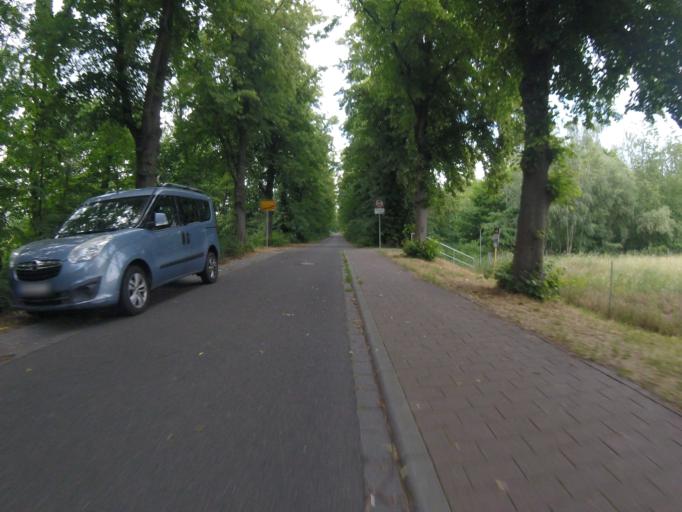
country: DE
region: Brandenburg
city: Konigs Wusterhausen
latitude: 52.3036
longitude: 13.5891
